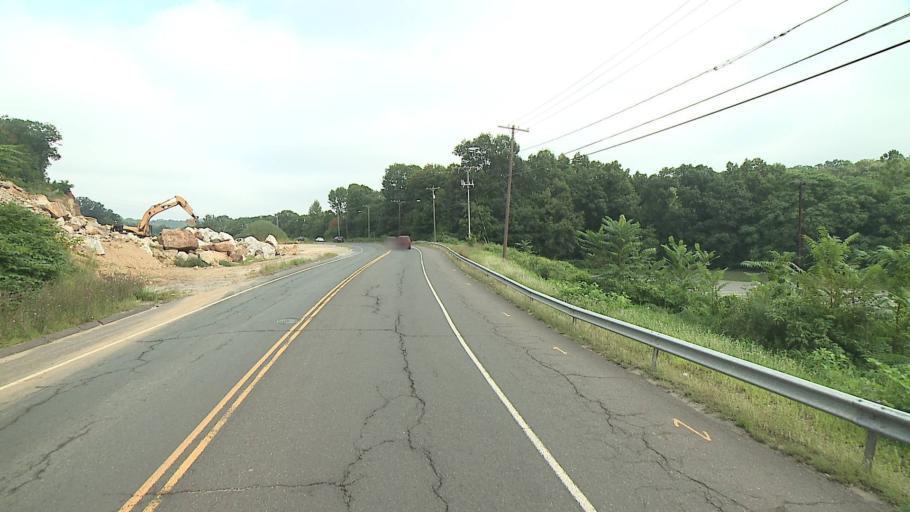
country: US
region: Connecticut
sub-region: Litchfield County
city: Oakville
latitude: 41.5805
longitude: -73.0717
